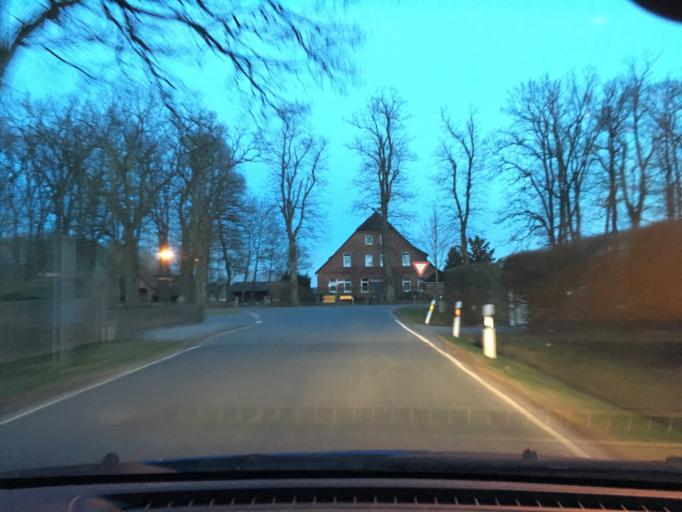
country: DE
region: Lower Saxony
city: Eyendorf
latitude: 53.1965
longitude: 10.1941
